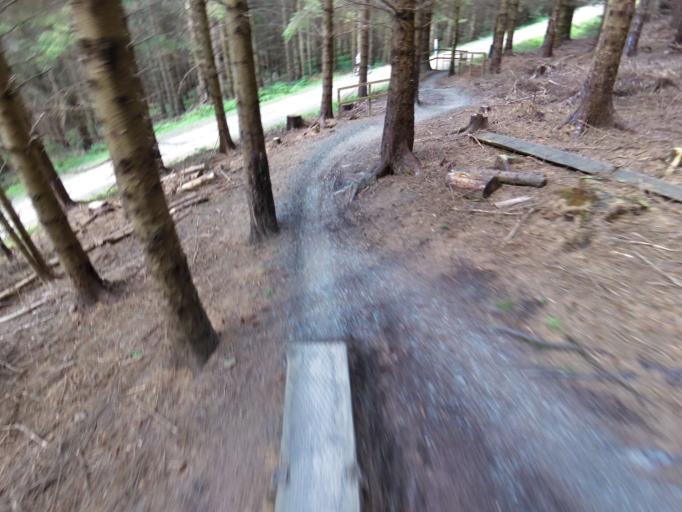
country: GB
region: Scotland
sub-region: The Scottish Borders
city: Peebles
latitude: 55.6589
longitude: -3.1310
